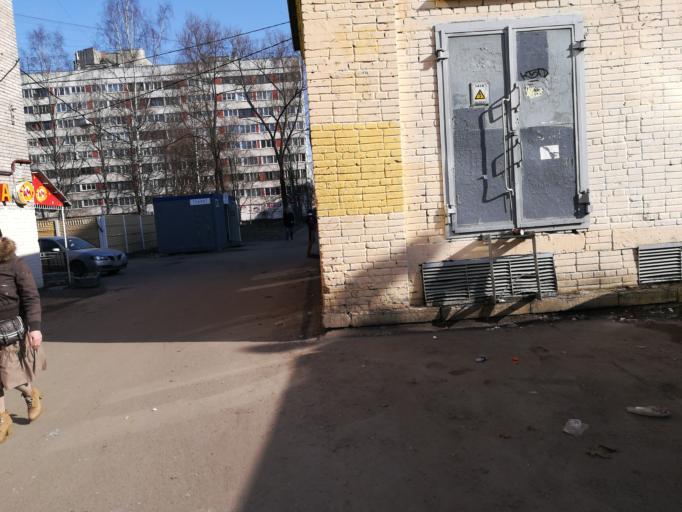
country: RU
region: St.-Petersburg
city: Vasyl'evsky Ostrov
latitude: 59.9493
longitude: 30.2345
